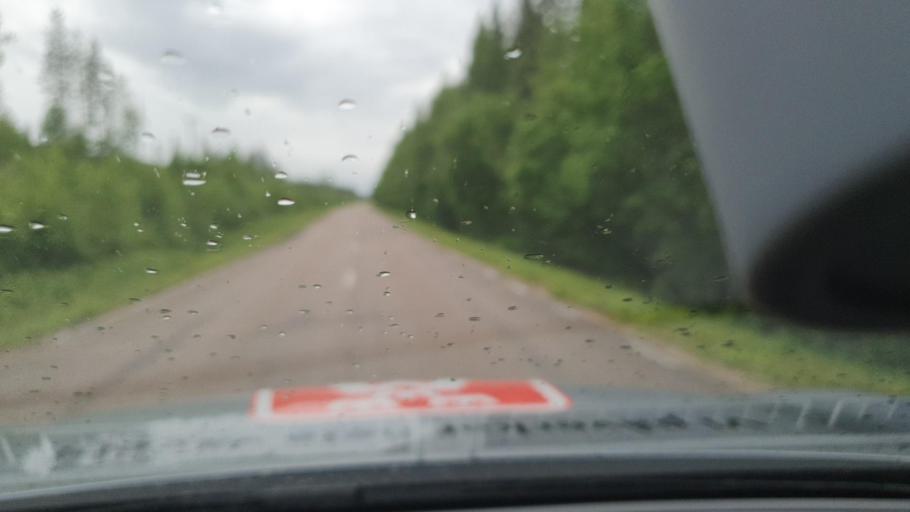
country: SE
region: Norrbotten
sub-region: Overkalix Kommun
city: OEverkalix
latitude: 66.4412
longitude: 22.7731
